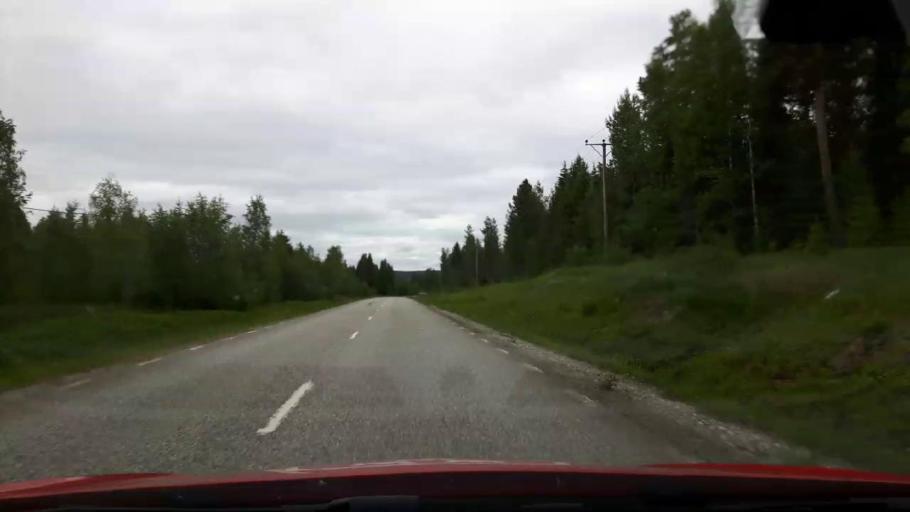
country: SE
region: Jaemtland
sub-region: Stroemsunds Kommun
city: Stroemsund
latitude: 63.3150
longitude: 15.7625
